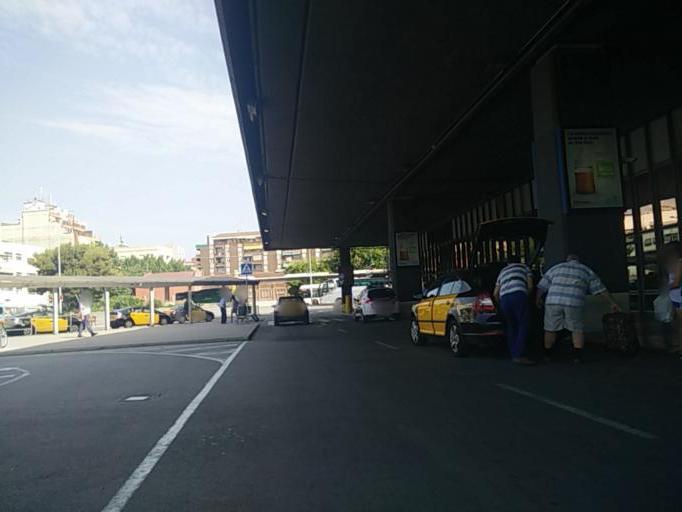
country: ES
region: Catalonia
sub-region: Provincia de Barcelona
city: les Corts
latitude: 41.3788
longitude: 2.1394
